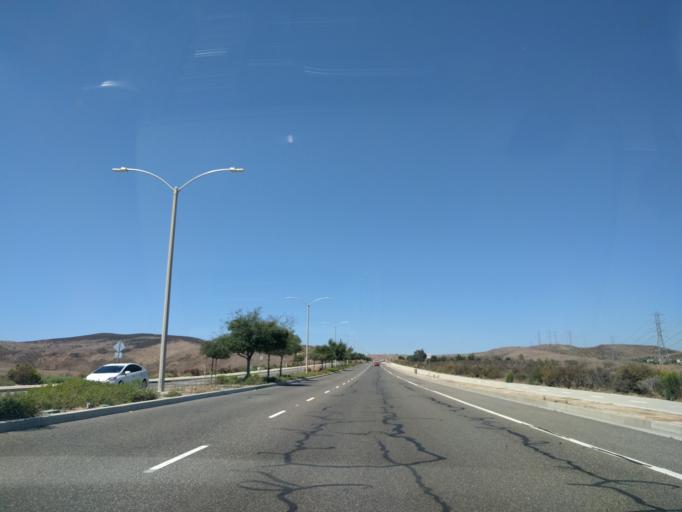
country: US
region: California
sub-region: Orange County
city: San Clemente
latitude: 33.4655
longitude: -117.6057
